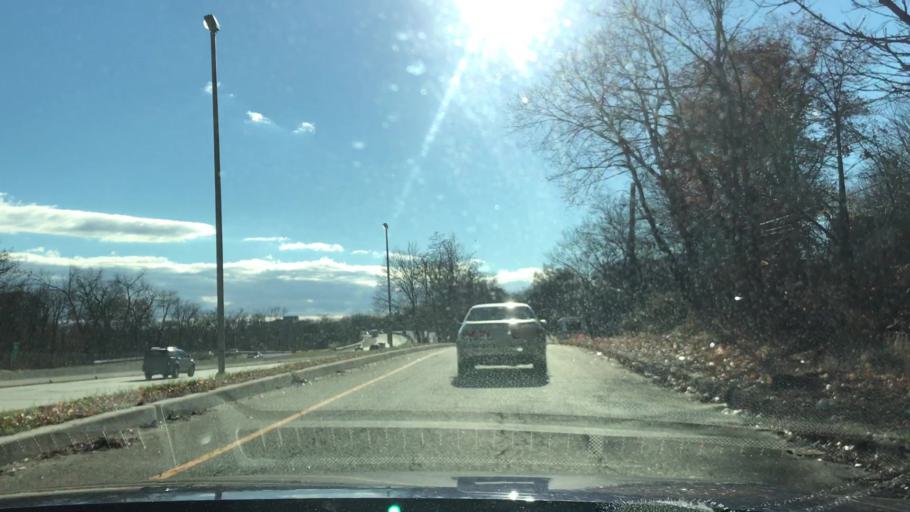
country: US
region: New Jersey
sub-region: Bergen County
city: Wallington
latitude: 40.8425
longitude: -74.1239
